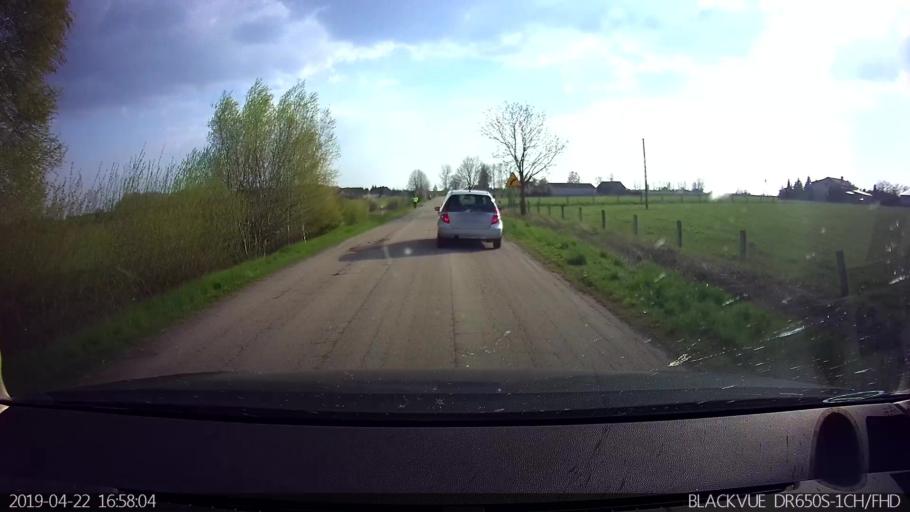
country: PL
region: Podlasie
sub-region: Powiat siemiatycki
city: Siemiatycze
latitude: 52.4738
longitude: 22.7539
